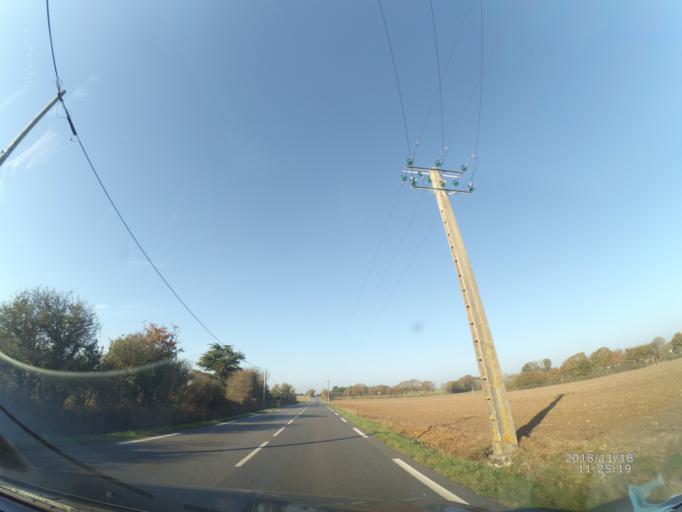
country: FR
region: Pays de la Loire
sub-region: Departement de la Loire-Atlantique
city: Saint-Michel-Chef-Chef
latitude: 47.2204
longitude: -2.1183
